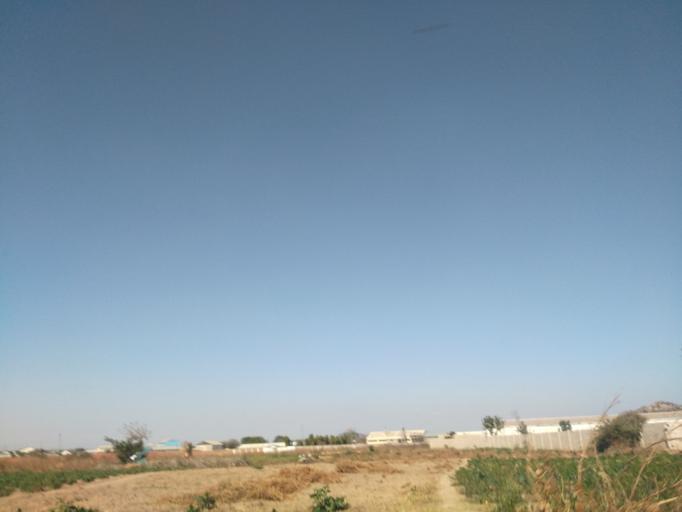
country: TZ
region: Dodoma
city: Dodoma
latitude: -6.1695
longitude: 35.7003
